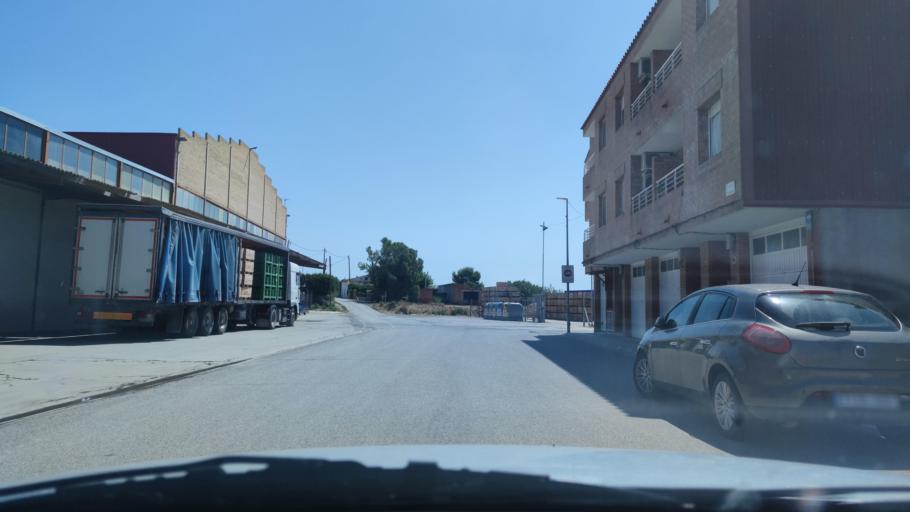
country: ES
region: Catalonia
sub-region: Provincia de Lleida
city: Alpicat
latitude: 41.6682
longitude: 0.5579
